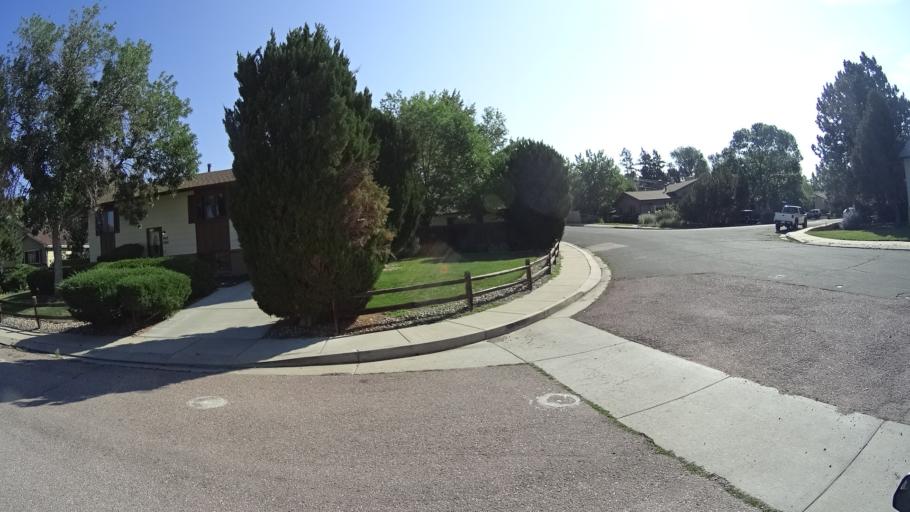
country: US
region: Colorado
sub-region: El Paso County
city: Colorado Springs
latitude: 38.8873
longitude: -104.8396
